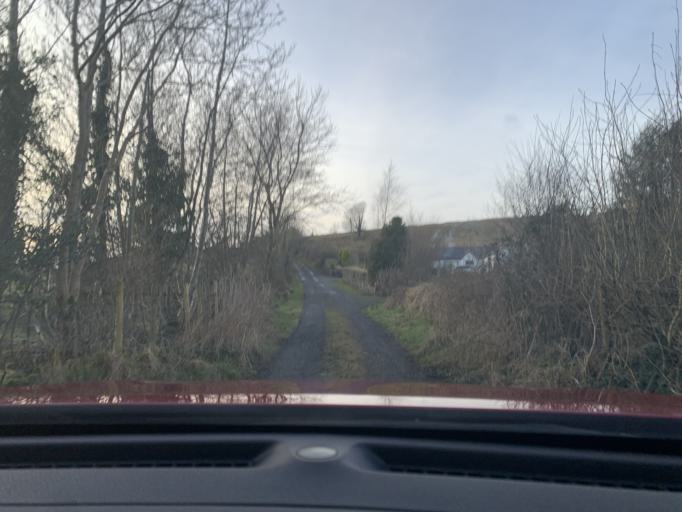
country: IE
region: Connaught
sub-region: Sligo
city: Strandhill
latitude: 54.1688
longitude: -8.6512
